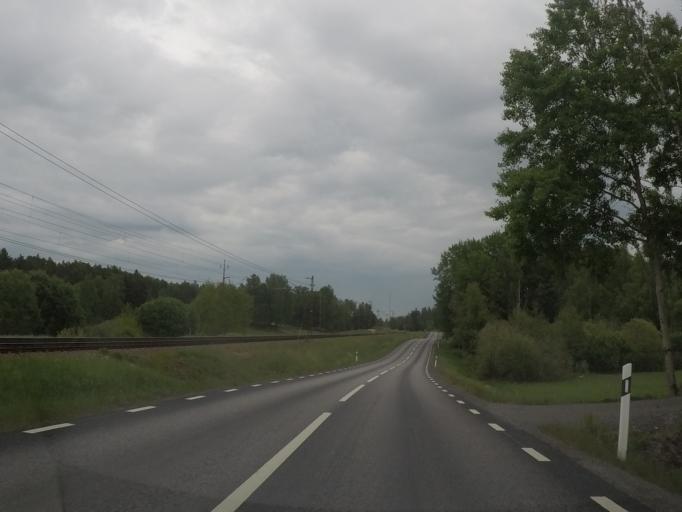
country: SE
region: Soedermanland
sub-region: Flens Kommun
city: Malmkoping
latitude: 59.0680
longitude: 16.7720
